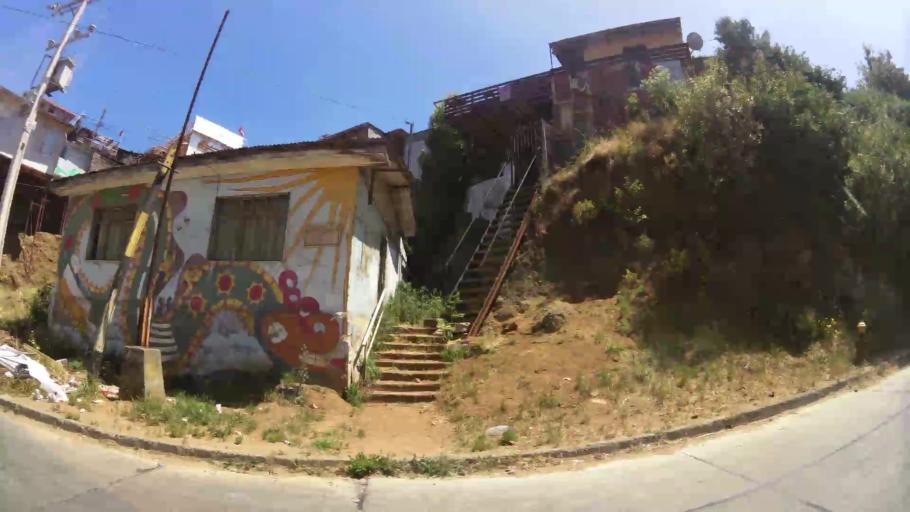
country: CL
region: Valparaiso
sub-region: Provincia de Valparaiso
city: Valparaiso
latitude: -33.0395
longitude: -71.6385
